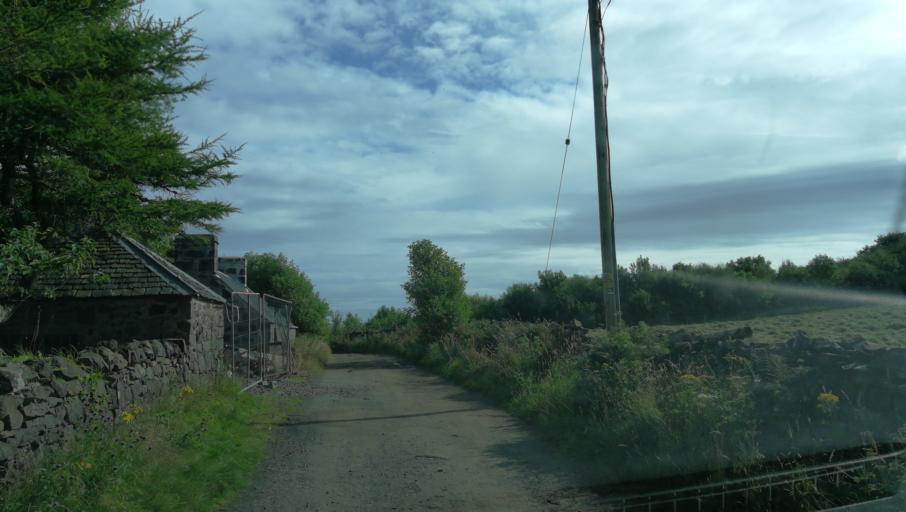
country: GB
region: Scotland
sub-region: Highland
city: Isle of Skye
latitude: 57.3953
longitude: -6.5672
